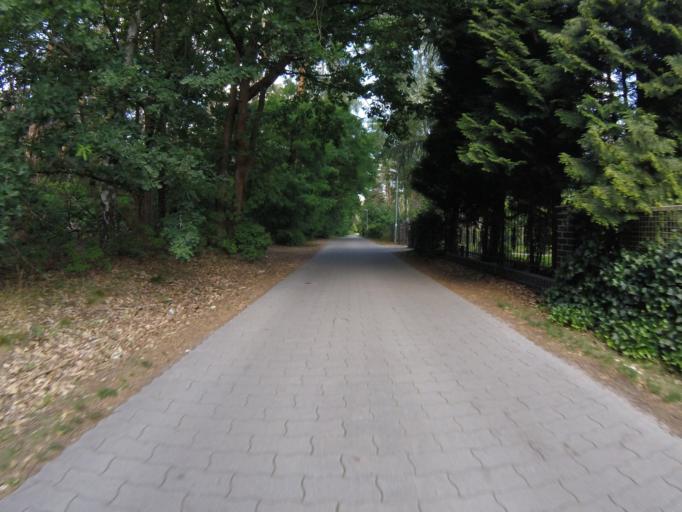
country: DE
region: Brandenburg
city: Bestensee
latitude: 52.2515
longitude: 13.6457
